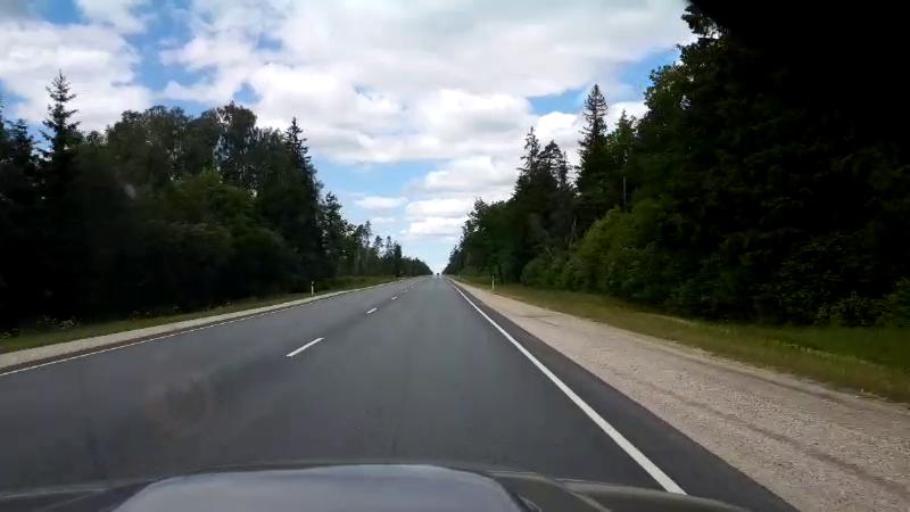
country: EE
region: Raplamaa
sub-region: Maerjamaa vald
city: Marjamaa
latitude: 58.9946
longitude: 24.4649
